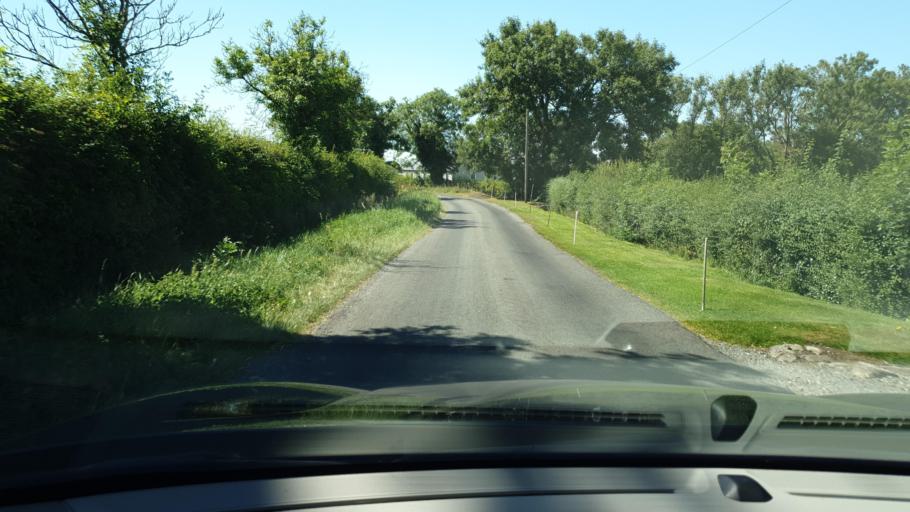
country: IE
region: Leinster
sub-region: An Mhi
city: Ashbourne
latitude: 53.4618
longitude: -6.4205
